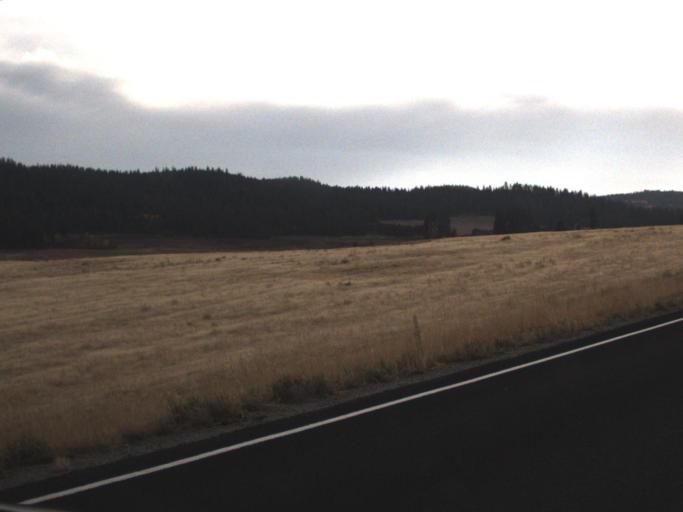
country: US
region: Washington
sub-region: Lincoln County
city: Davenport
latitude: 48.0121
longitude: -118.2495
